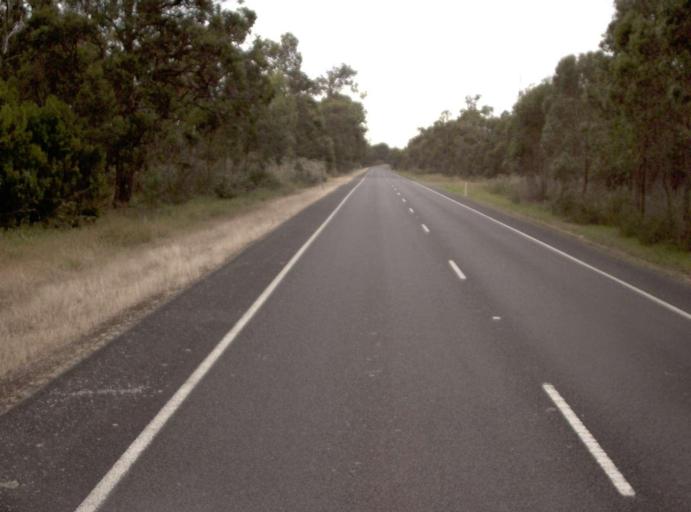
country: AU
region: Victoria
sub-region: Wellington
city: Sale
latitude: -38.3550
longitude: 146.9957
